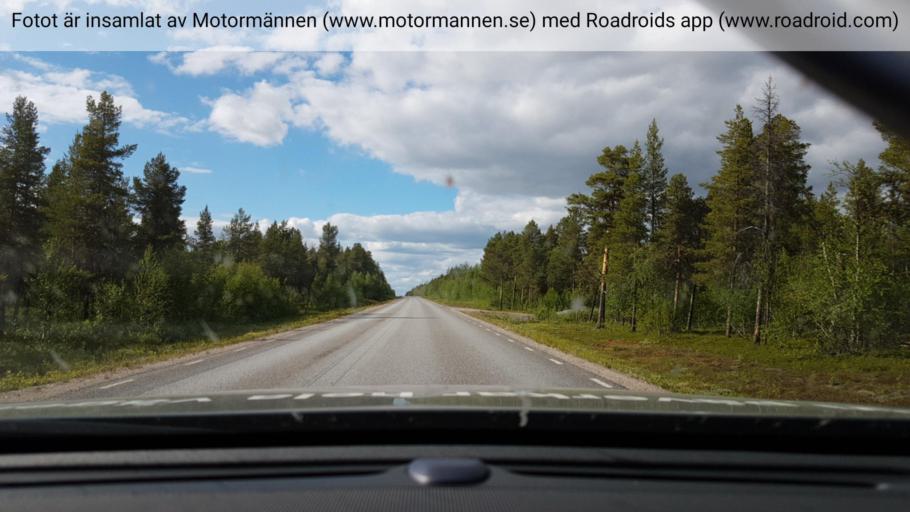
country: SE
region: Norrbotten
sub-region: Arjeplogs Kommun
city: Arjeplog
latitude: 66.1710
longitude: 17.3272
